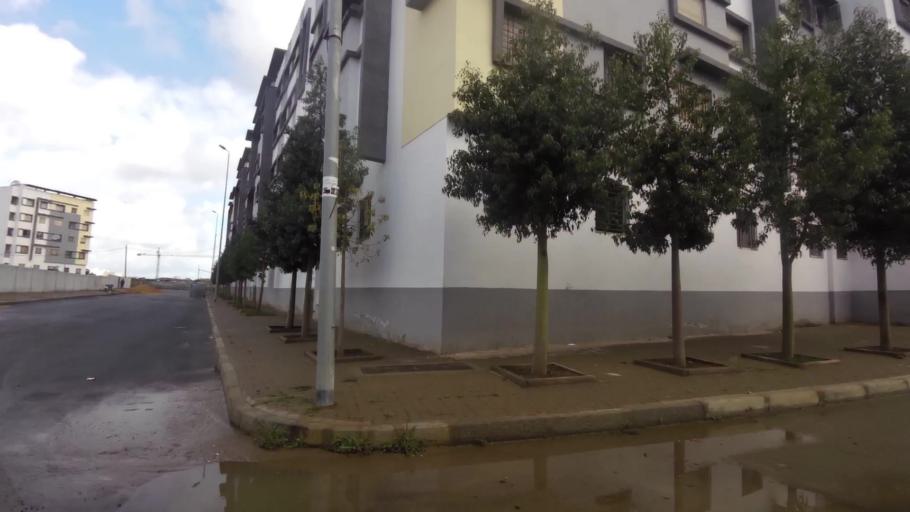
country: MA
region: Grand Casablanca
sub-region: Casablanca
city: Casablanca
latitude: 33.5439
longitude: -7.6911
